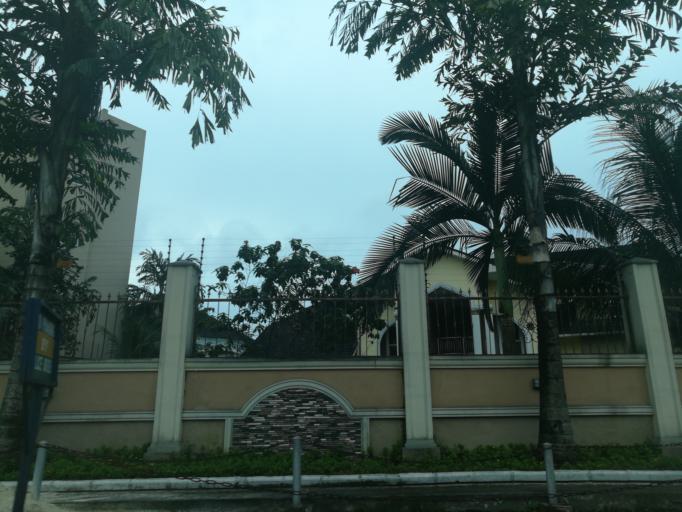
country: NG
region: Rivers
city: Port Harcourt
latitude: 4.8232
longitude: 6.9926
